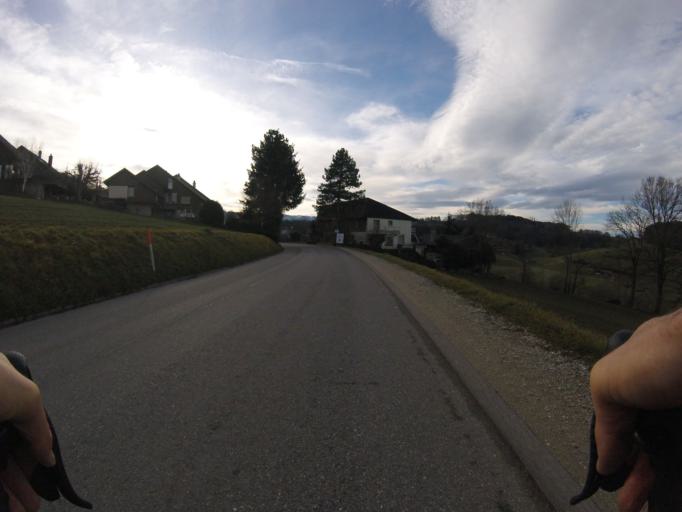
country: CH
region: Fribourg
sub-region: Sense District
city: Ueberstorf
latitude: 46.8544
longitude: 7.3156
